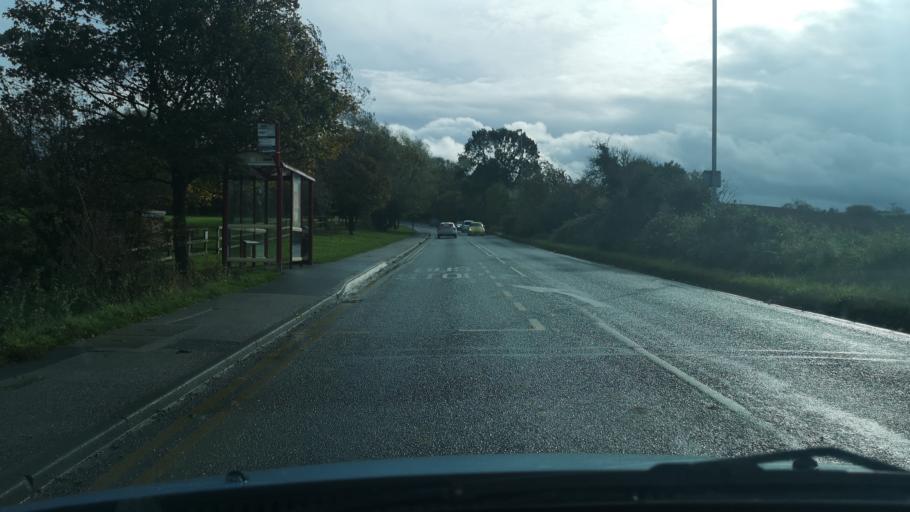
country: GB
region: England
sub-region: City and Borough of Wakefield
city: Hemsworth
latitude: 53.6223
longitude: -1.3645
